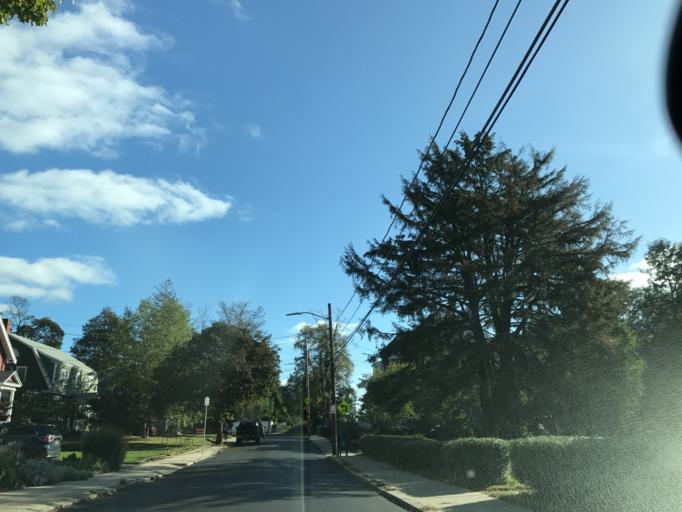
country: US
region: Massachusetts
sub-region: Suffolk County
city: South Boston
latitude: 42.3090
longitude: -71.0481
